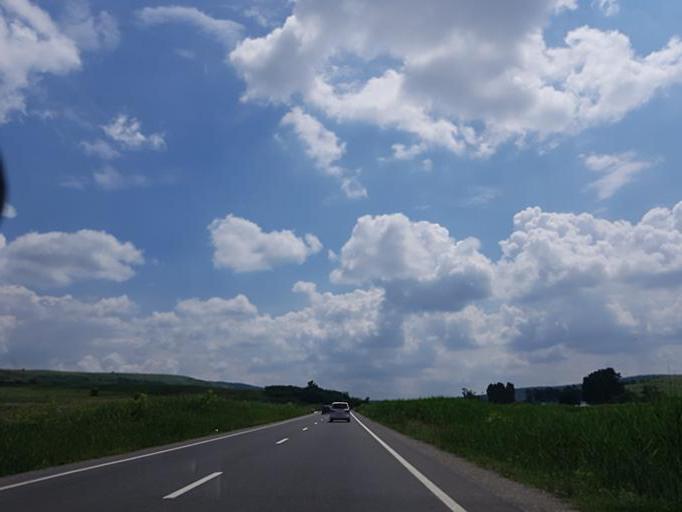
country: RO
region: Sibiu
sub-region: Comuna Seica Mare
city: Seica Mare
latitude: 45.9714
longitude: 24.1511
